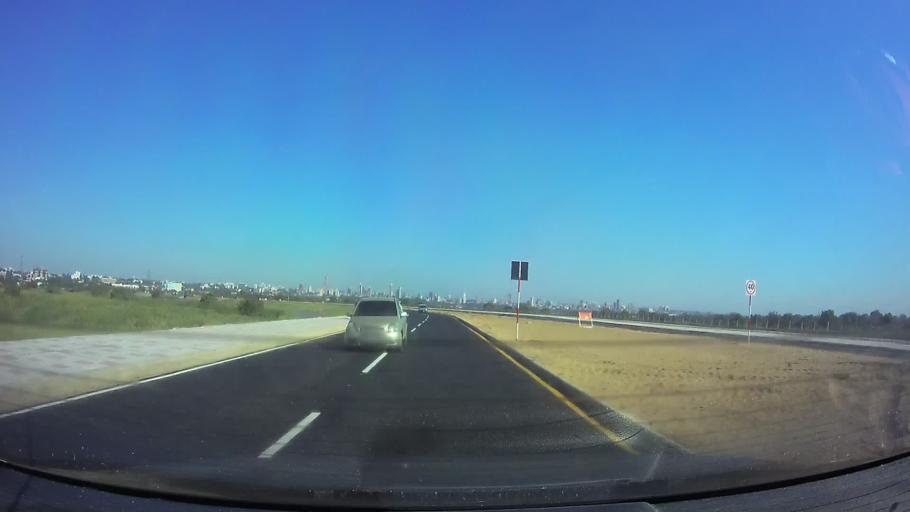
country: PY
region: Asuncion
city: Asuncion
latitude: -25.2535
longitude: -57.6063
